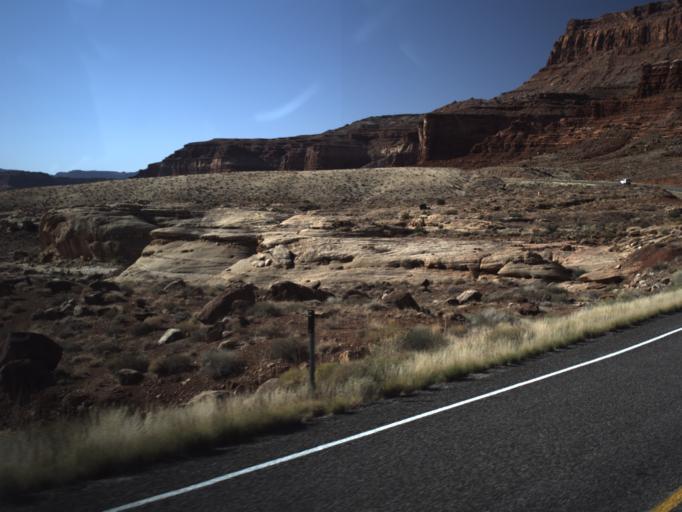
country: US
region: Utah
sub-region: San Juan County
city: Blanding
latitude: 37.9208
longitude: -110.3962
